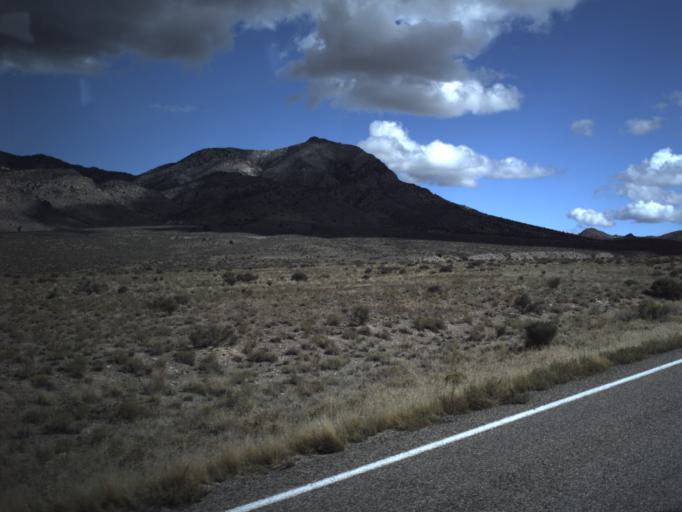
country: US
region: Utah
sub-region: Beaver County
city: Milford
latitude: 38.4417
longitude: -113.3200
